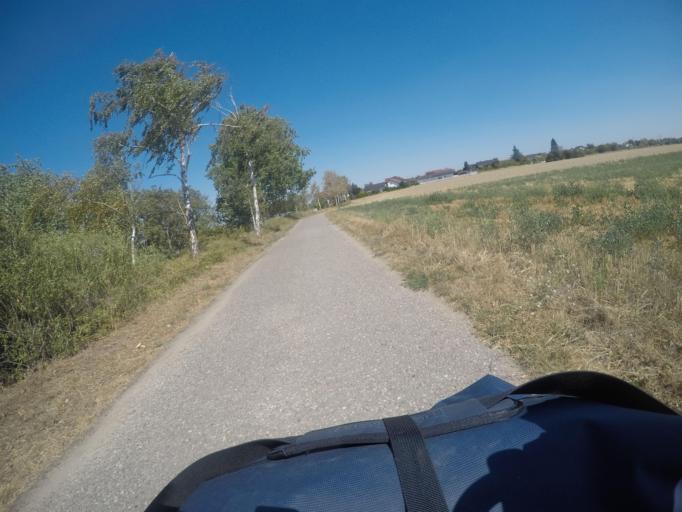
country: DE
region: Baden-Wuerttemberg
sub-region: Karlsruhe Region
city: Oberhausen-Rheinhausen
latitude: 49.2504
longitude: 8.4811
